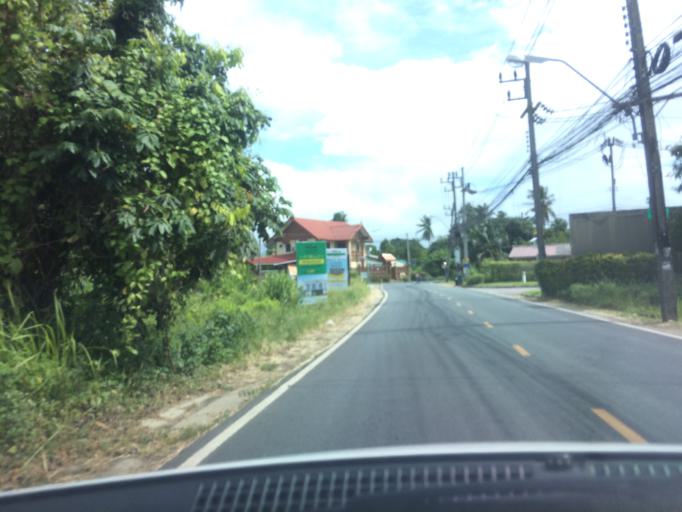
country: TH
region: Phuket
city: Thalang
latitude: 8.0304
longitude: 98.3409
